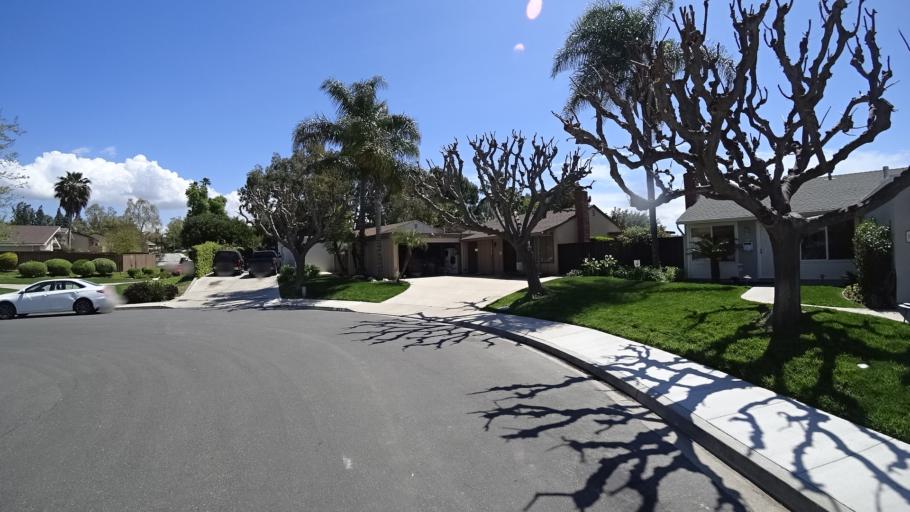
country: US
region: California
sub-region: Ventura County
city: Thousand Oaks
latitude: 34.2139
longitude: -118.8445
